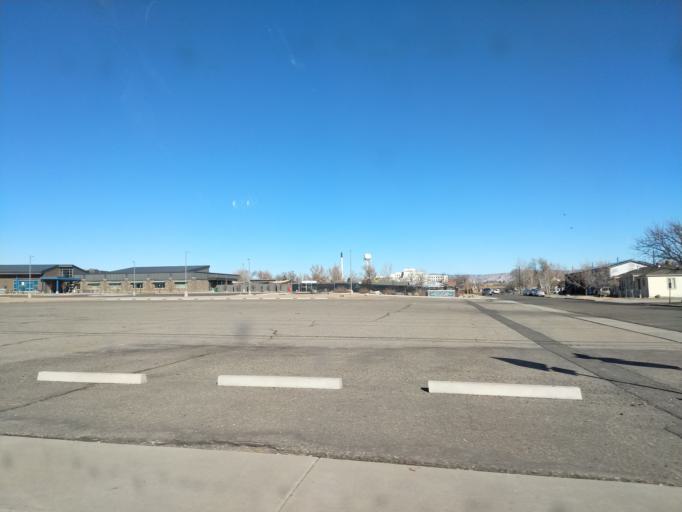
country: US
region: Colorado
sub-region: Mesa County
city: Grand Junction
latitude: 39.0702
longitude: -108.5396
